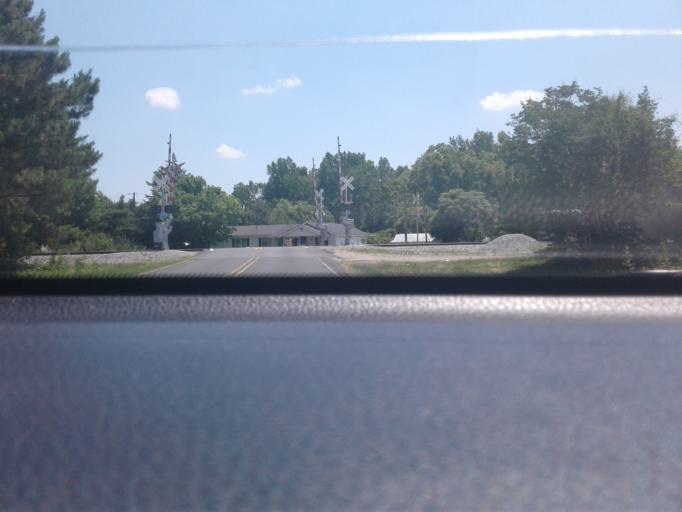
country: US
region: North Carolina
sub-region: Harnett County
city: Dunn
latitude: 35.3428
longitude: -78.5815
